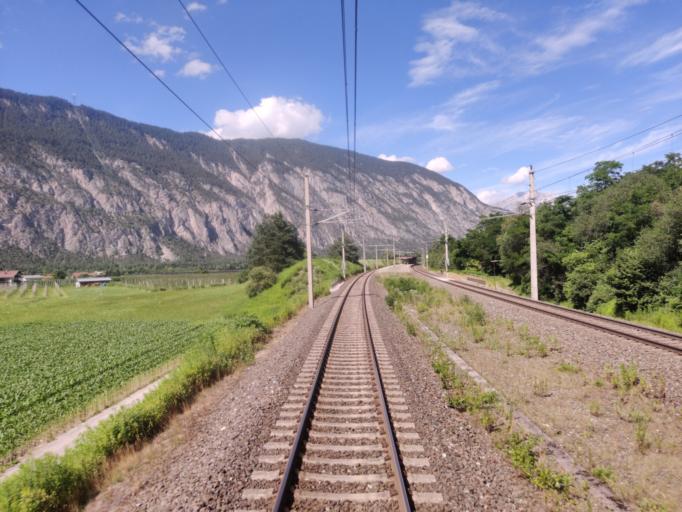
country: AT
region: Tyrol
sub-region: Politischer Bezirk Imst
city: Haiming
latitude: 47.2510
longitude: 10.8874
